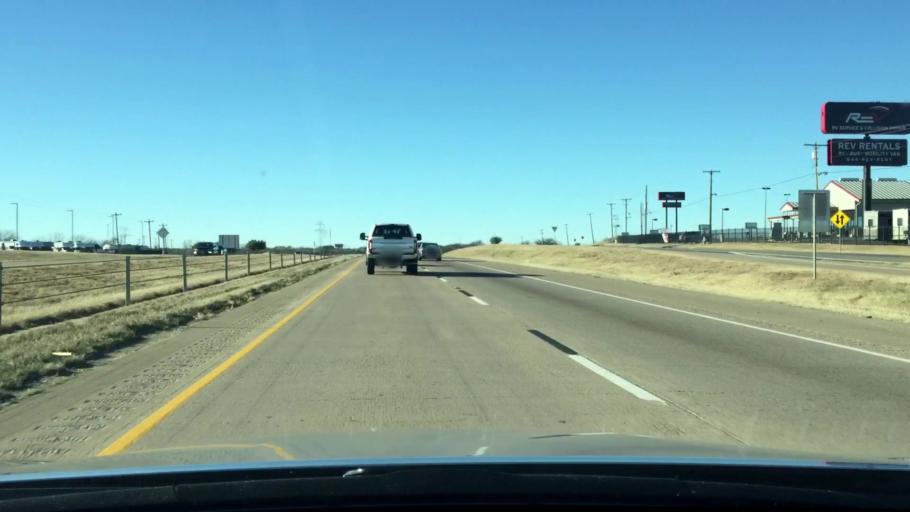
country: US
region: Texas
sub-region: Johnson County
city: Alvarado
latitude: 32.4271
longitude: -97.2349
